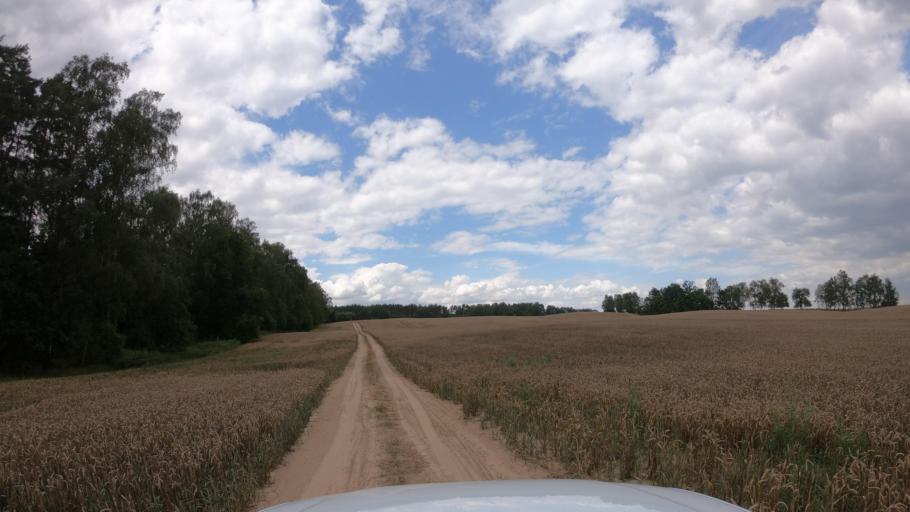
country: PL
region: West Pomeranian Voivodeship
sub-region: Powiat stargardzki
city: Dolice
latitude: 53.2004
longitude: 15.2848
